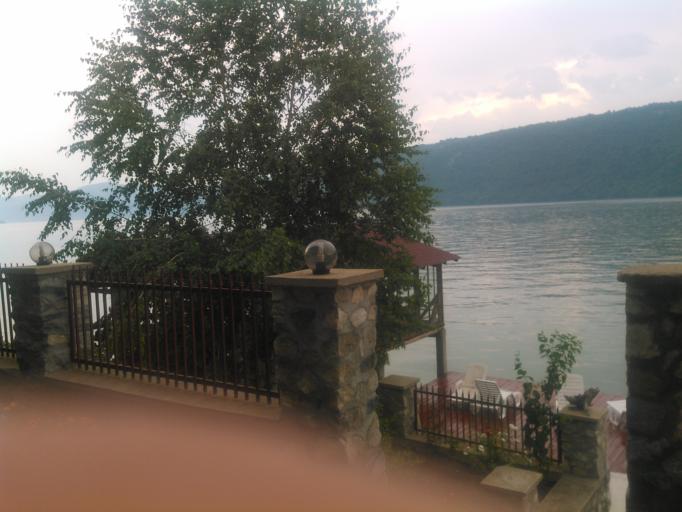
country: RO
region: Mehedinti
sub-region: Comuna Eselnita
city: Eselnita
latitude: 44.6703
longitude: 22.3091
